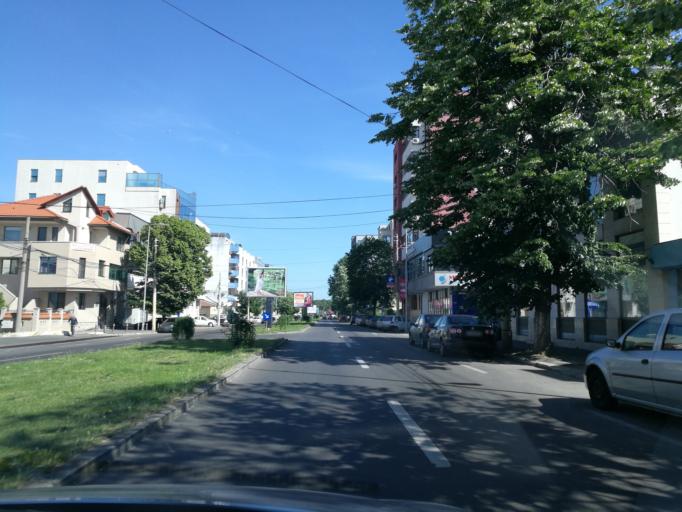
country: RO
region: Constanta
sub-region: Municipiul Constanta
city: Constanta
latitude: 44.2021
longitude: 28.6456
